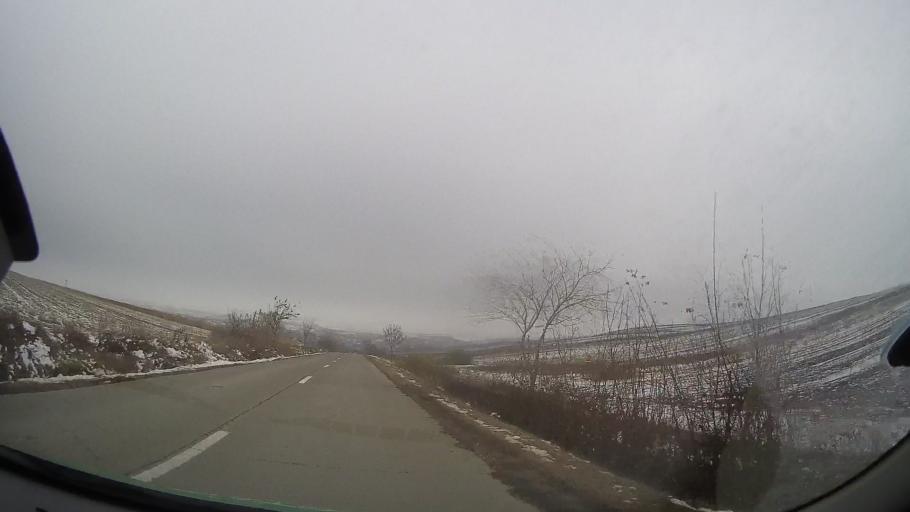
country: RO
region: Vaslui
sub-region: Comuna Ivesti
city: Ivesti
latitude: 46.1967
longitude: 27.5174
